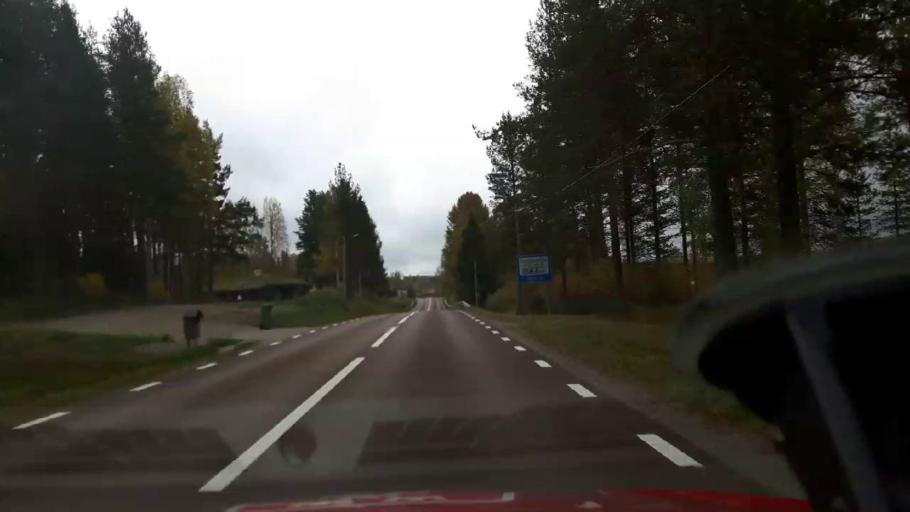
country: SE
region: Jaemtland
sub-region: Harjedalens Kommun
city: Sveg
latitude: 62.2965
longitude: 14.7830
